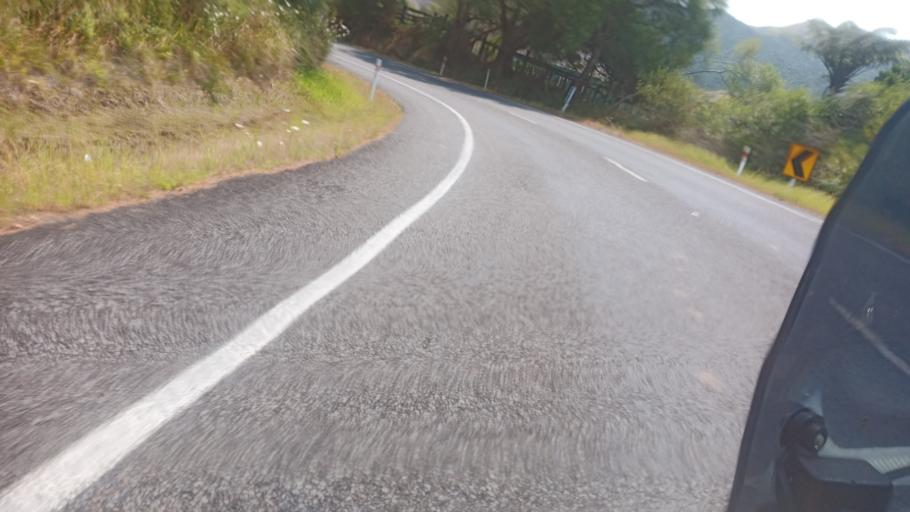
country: NZ
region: Bay of Plenty
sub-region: Opotiki District
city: Opotiki
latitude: -37.5710
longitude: 178.0533
